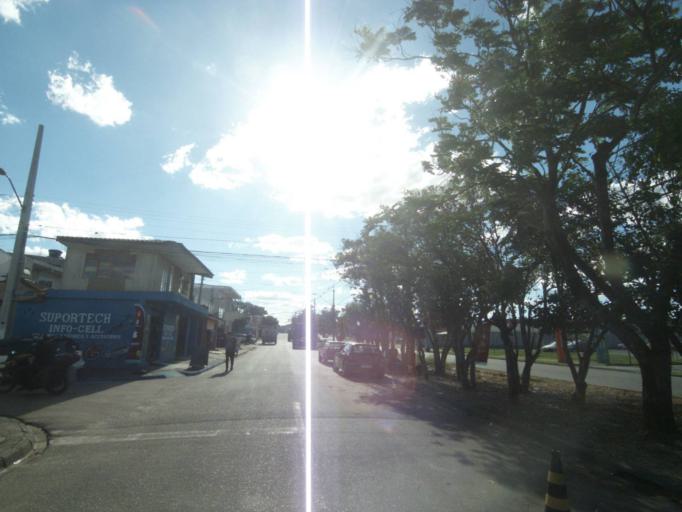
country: BR
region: Parana
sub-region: Curitiba
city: Curitiba
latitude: -25.4978
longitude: -49.3392
